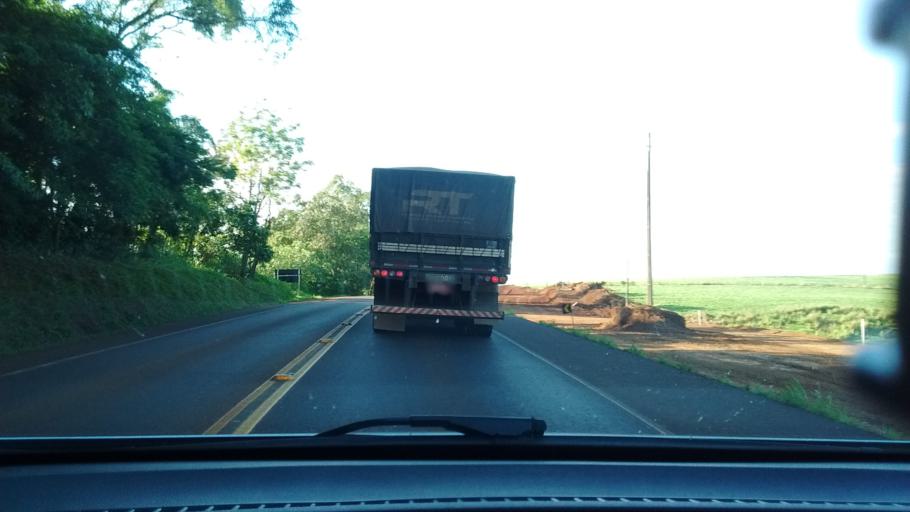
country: BR
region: Parana
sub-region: Cascavel
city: Cascavel
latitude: -25.2168
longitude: -53.5954
